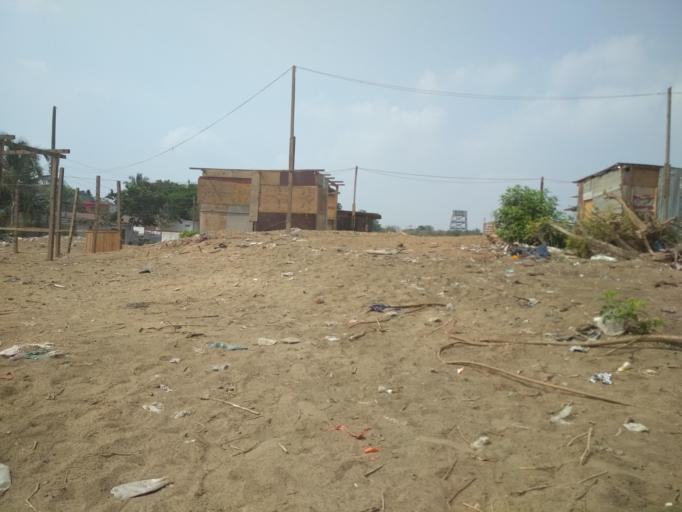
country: MX
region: Veracruz
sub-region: Veracruz
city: Rio Medio [Granja]
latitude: 19.2113
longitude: -96.2104
